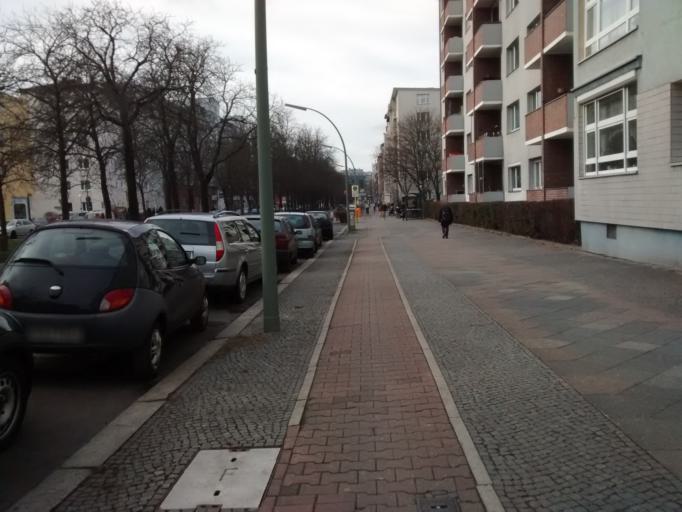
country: DE
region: Berlin
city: Hansaviertel
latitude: 52.5203
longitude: 13.3368
